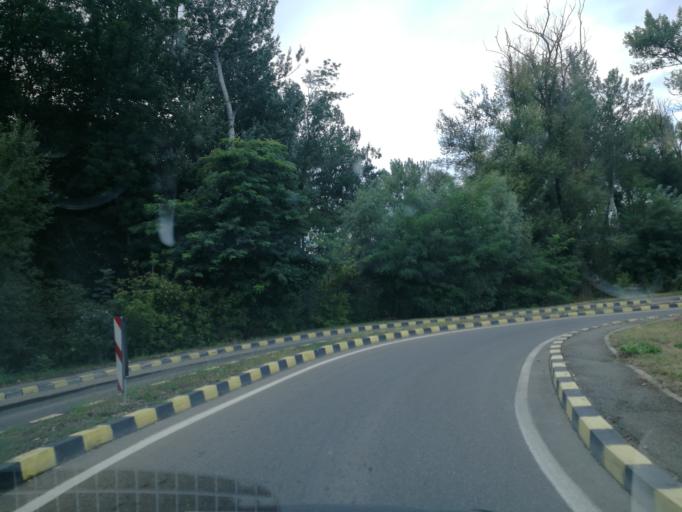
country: RO
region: Suceava
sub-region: Comuna Scheia
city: Scheia
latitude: 47.6637
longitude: 26.2469
